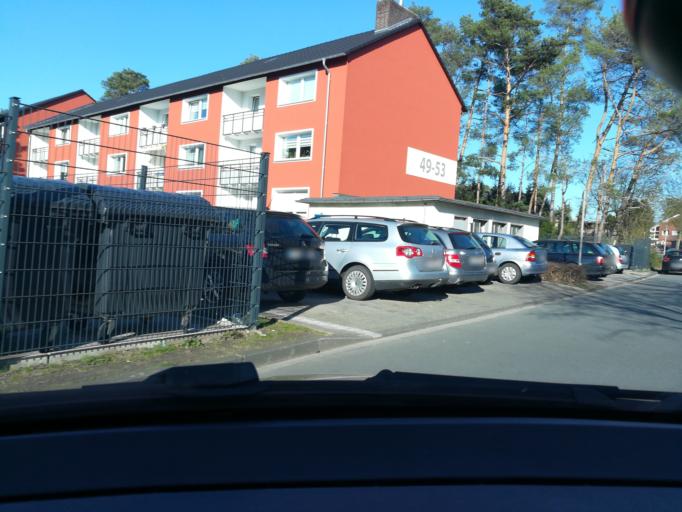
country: DE
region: North Rhine-Westphalia
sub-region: Regierungsbezirk Detmold
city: Oerlinghausen
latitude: 51.9513
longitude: 8.6000
